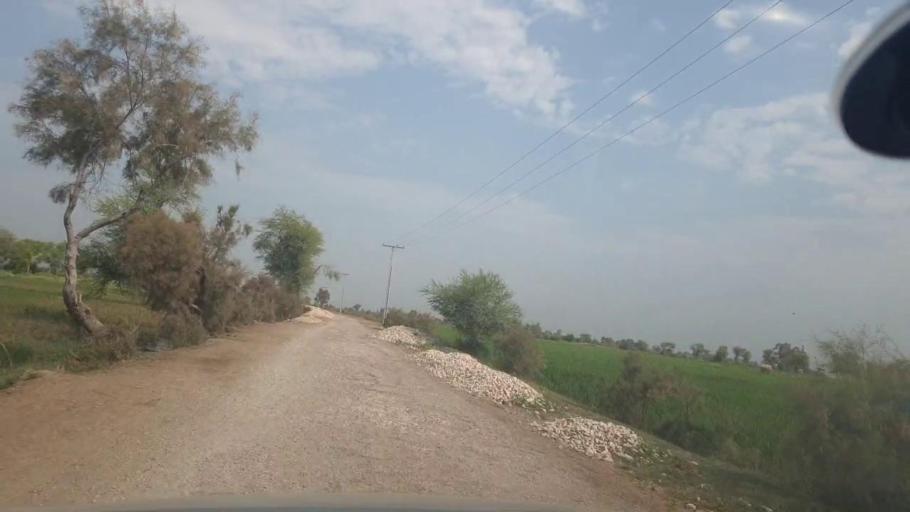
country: PK
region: Balochistan
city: Mehrabpur
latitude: 28.0664
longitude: 68.1034
